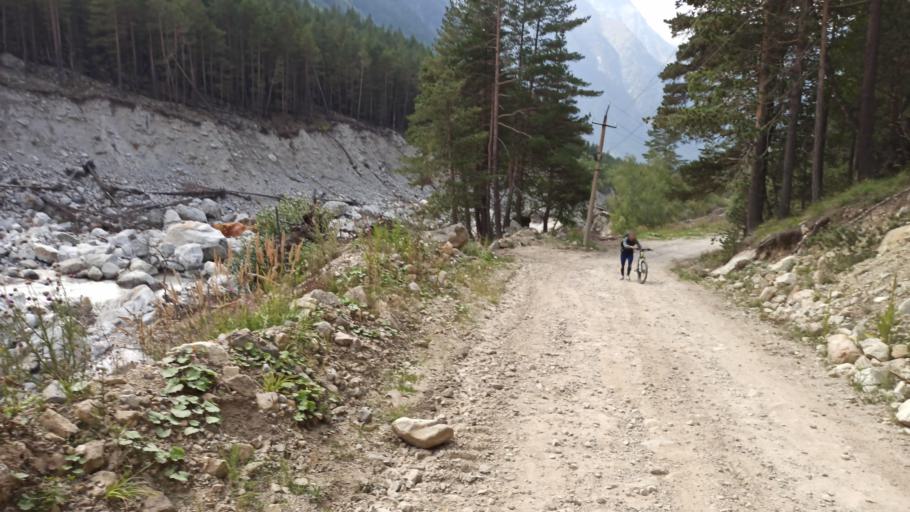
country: RU
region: Kabardino-Balkariya
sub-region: El'brusskiy Rayon
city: El'brus
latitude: 43.2197
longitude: 42.6892
